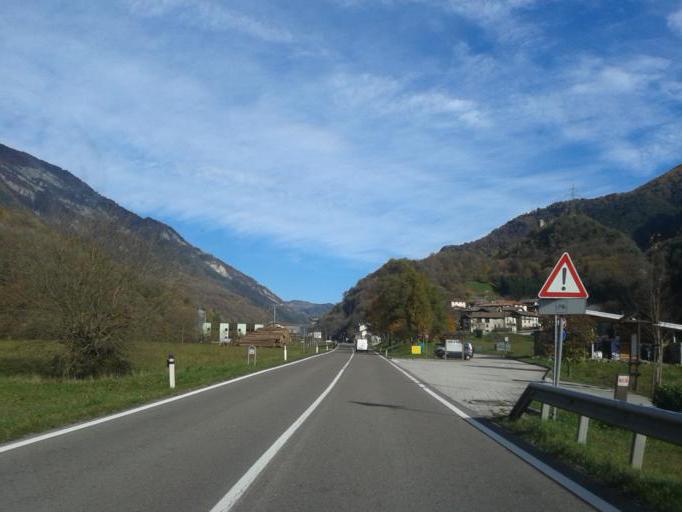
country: IT
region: Trentino-Alto Adige
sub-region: Provincia di Trento
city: Prezzo
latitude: 45.9273
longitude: 10.6347
